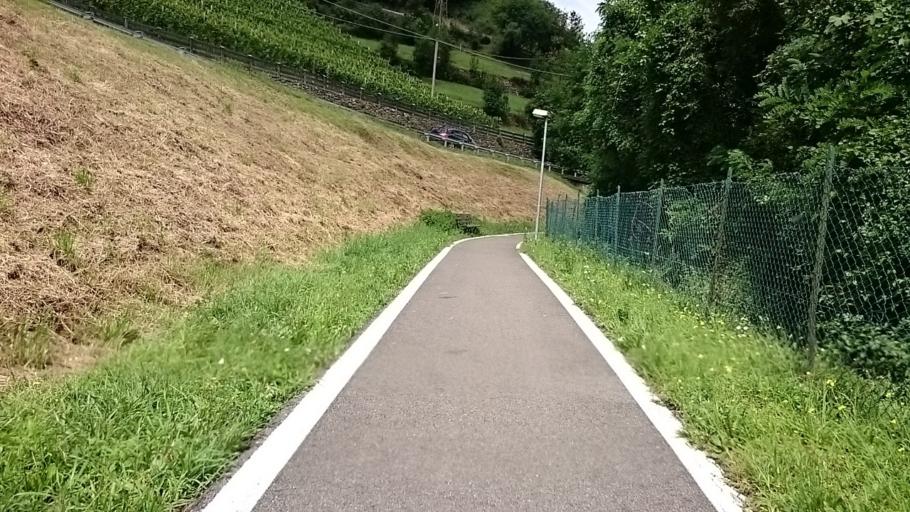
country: IT
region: Trentino-Alto Adige
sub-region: Bolzano
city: Ponte Gardena
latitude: 46.5925
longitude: 11.5264
